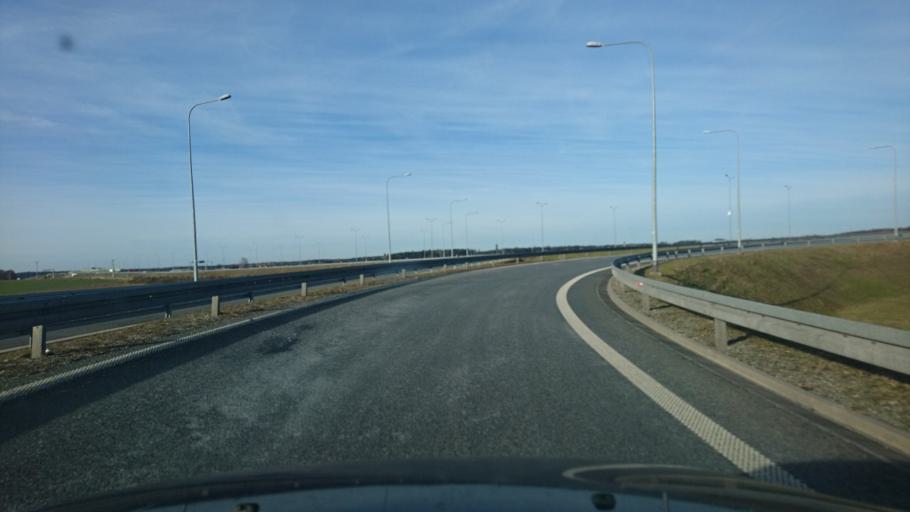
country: PL
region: Greater Poland Voivodeship
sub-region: Powiat kepinski
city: Kepno
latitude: 51.3146
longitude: 18.0075
